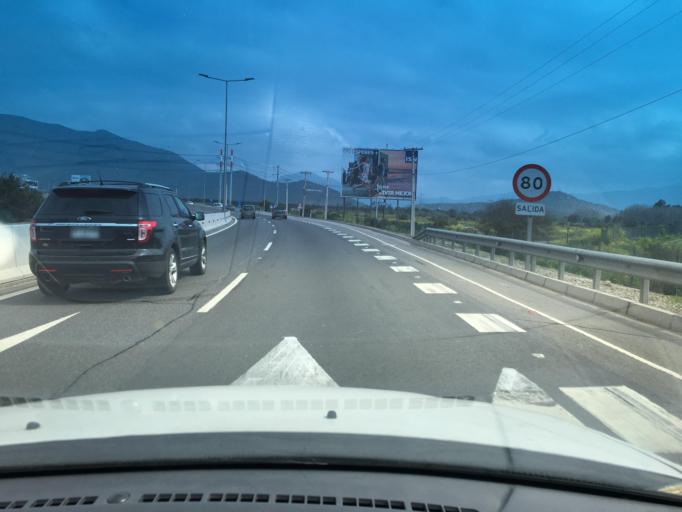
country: CL
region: Santiago Metropolitan
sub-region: Provincia de Santiago
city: Lo Prado
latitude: -33.4285
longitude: -70.8068
